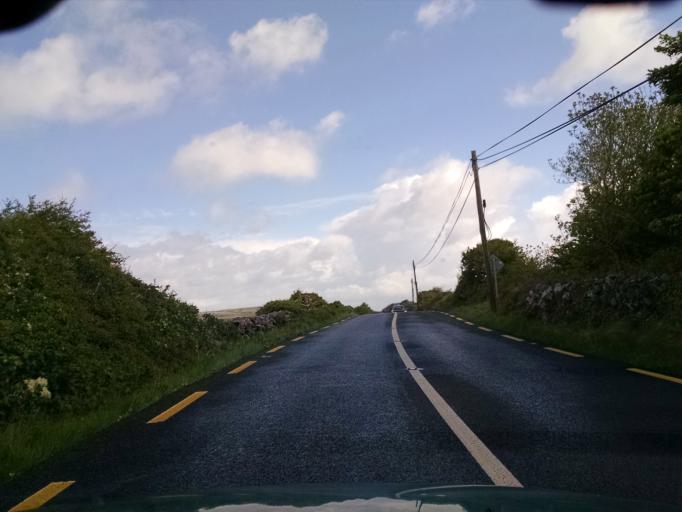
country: IE
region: Connaught
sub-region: County Galway
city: Bearna
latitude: 53.1289
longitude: -9.1214
